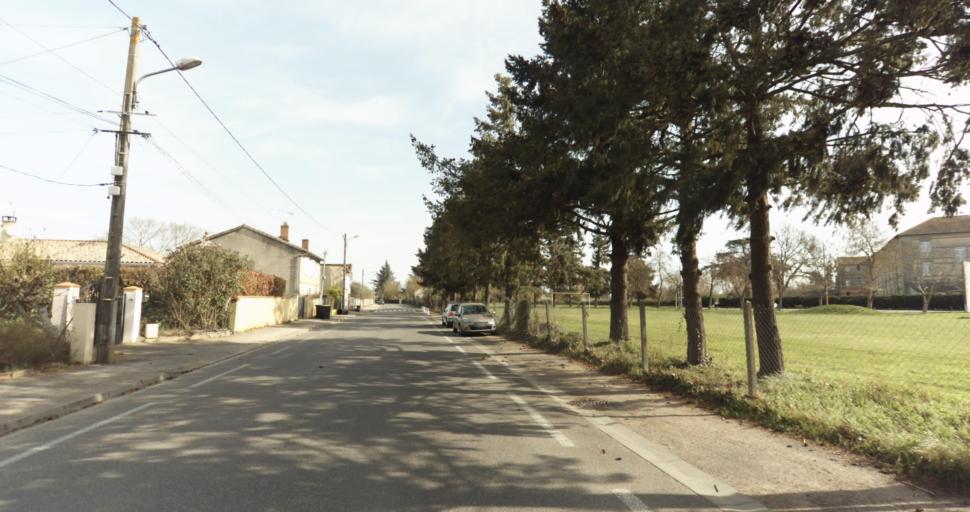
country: FR
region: Midi-Pyrenees
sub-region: Departement du Tarn
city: Saint-Sulpice-la-Pointe
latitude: 43.7775
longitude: 1.6803
